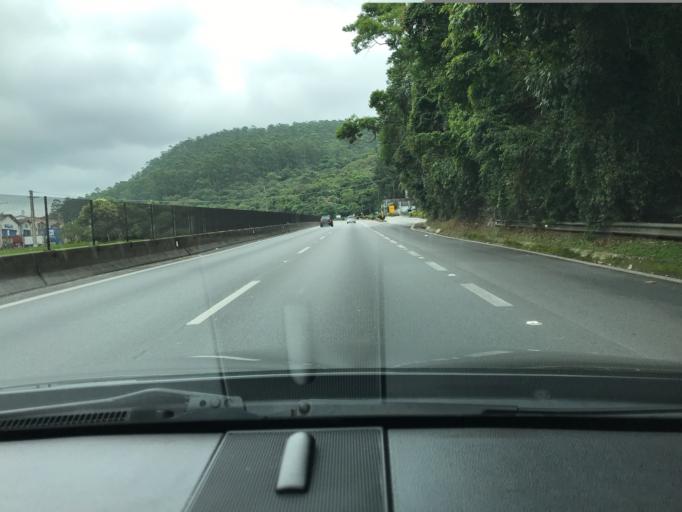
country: BR
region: Sao Paulo
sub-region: Cotia
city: Cotia
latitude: -23.6017
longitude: -46.9362
